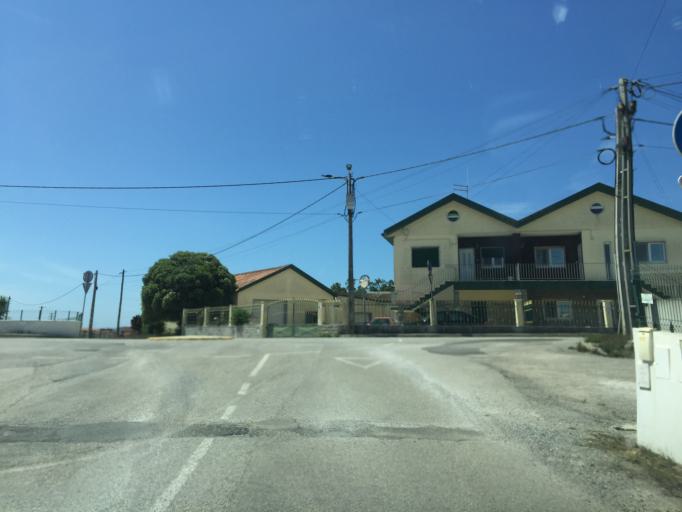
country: PT
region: Lisbon
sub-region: Lourinha
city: Lourinha
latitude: 39.2102
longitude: -9.3243
